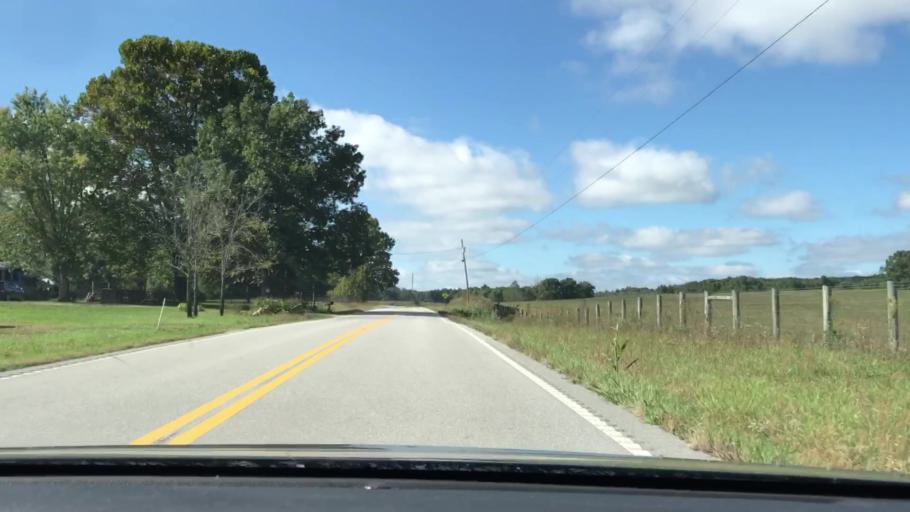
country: US
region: Tennessee
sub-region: Fentress County
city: Jamestown
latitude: 36.3610
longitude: -84.7424
